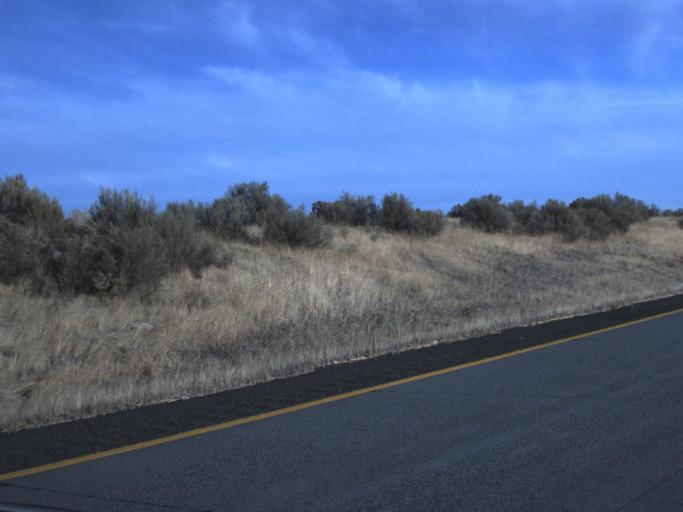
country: US
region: Washington
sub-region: Franklin County
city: Basin City
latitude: 46.5084
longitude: -119.0134
